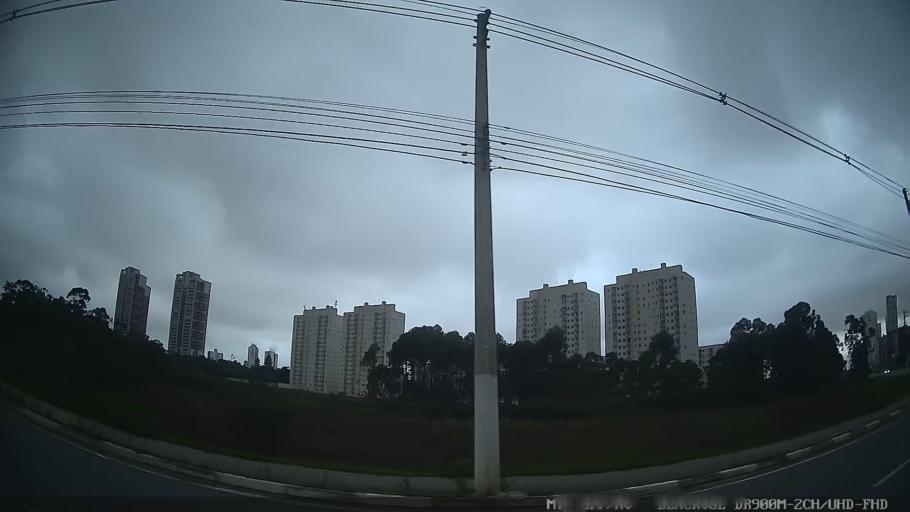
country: BR
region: Sao Paulo
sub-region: Mogi das Cruzes
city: Mogi das Cruzes
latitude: -23.5102
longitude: -46.1766
